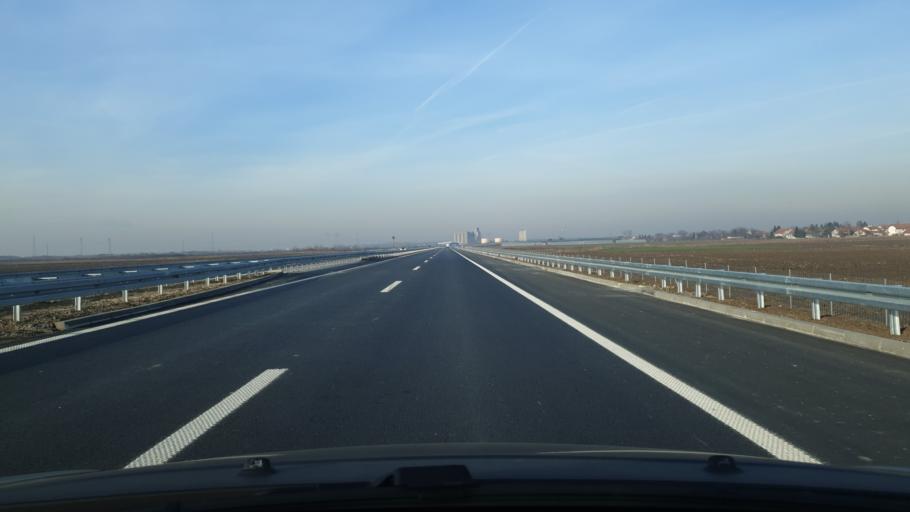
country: RS
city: Boljevci
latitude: 44.7546
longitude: 20.2487
